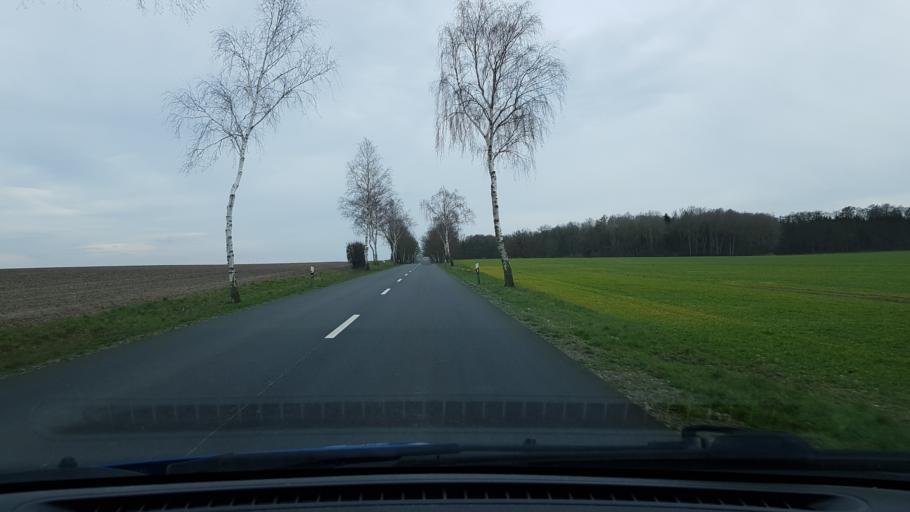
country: DE
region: Lower Saxony
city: Emmendorf
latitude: 53.0205
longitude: 10.6011
